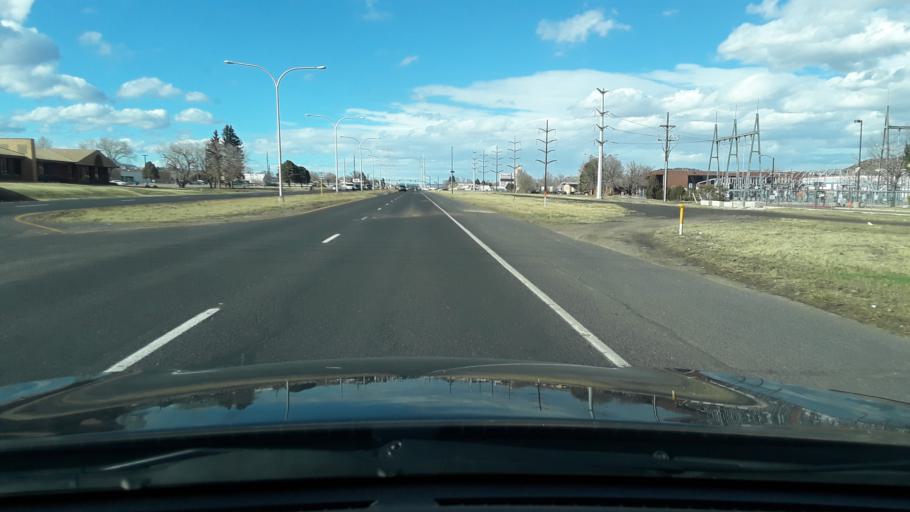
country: US
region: Colorado
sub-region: El Paso County
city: Colorado Springs
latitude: 38.8813
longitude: -104.8186
